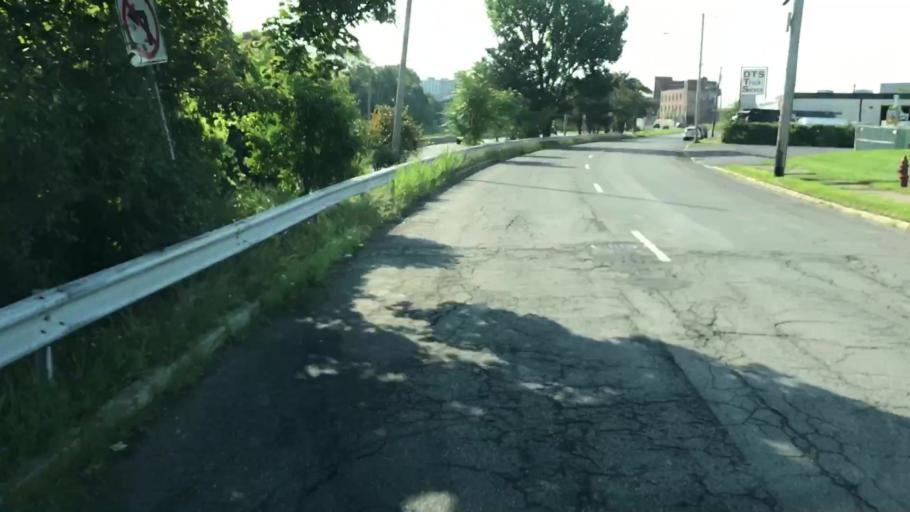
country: US
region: New York
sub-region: Onondaga County
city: Syracuse
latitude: 43.0641
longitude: -76.1600
